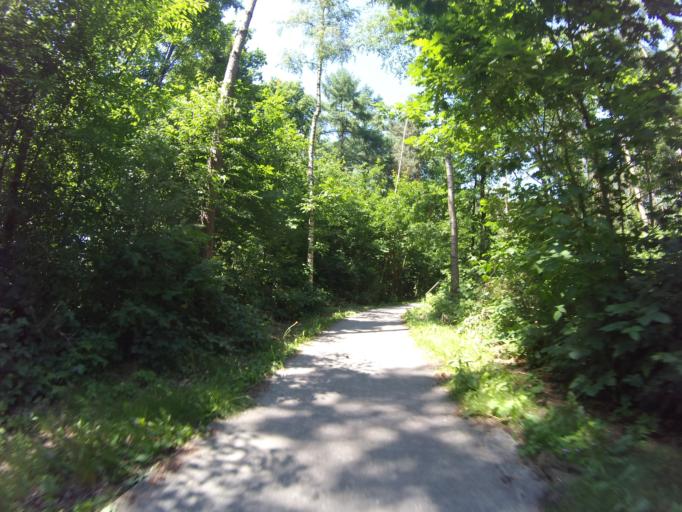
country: NL
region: Drenthe
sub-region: Gemeente Emmen
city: Emmen
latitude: 52.7858
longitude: 6.9163
